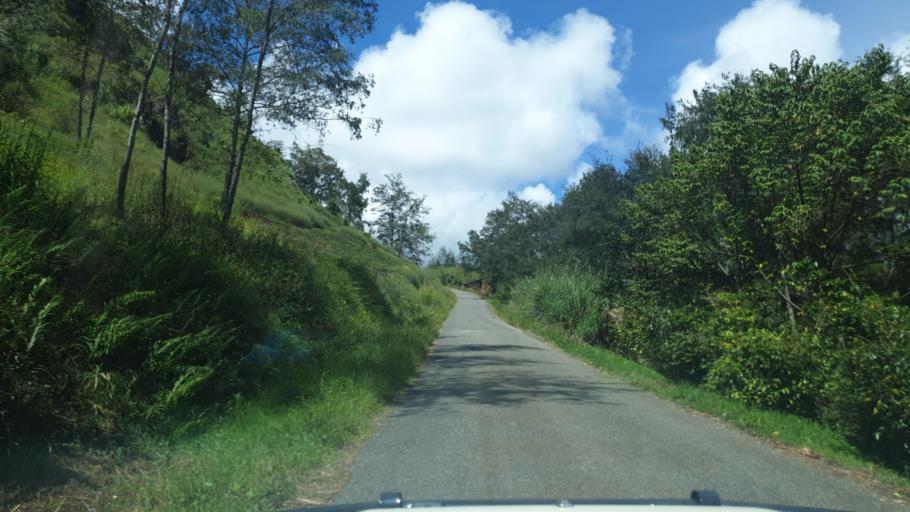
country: PG
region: Chimbu
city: Kundiawa
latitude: -6.1516
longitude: 145.1334
